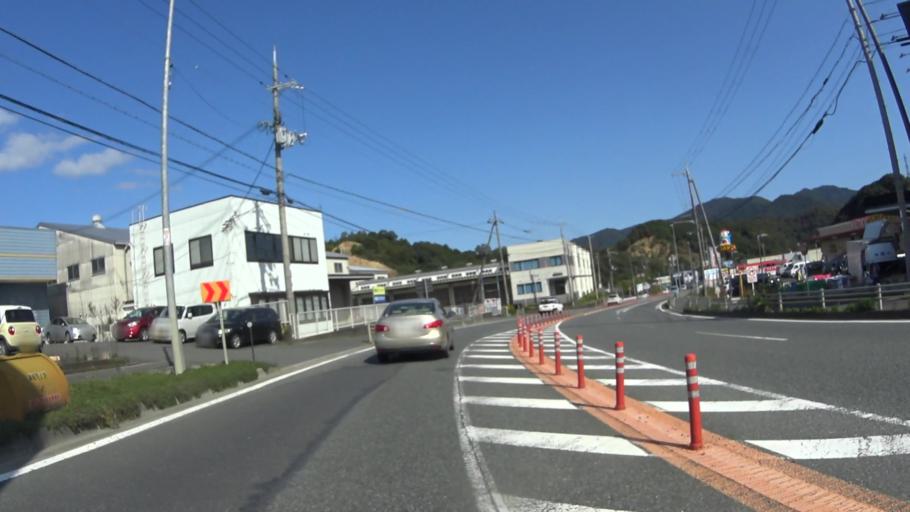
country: JP
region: Kyoto
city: Fukuchiyama
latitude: 35.3241
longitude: 135.0969
